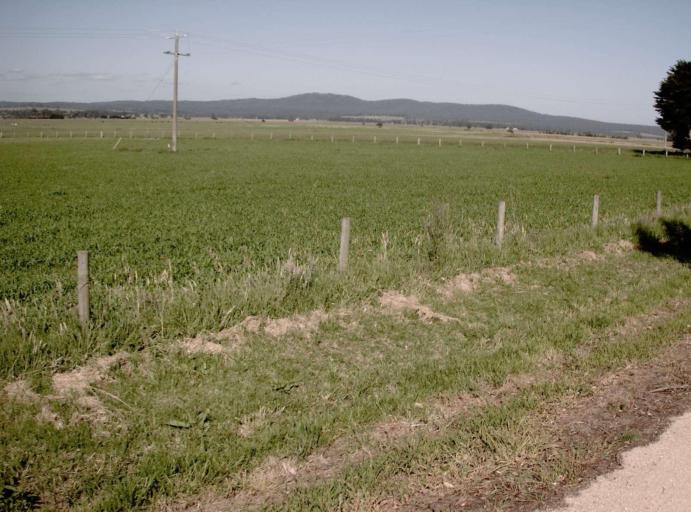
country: AU
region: Victoria
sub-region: East Gippsland
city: Lakes Entrance
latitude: -37.7239
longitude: 148.4977
